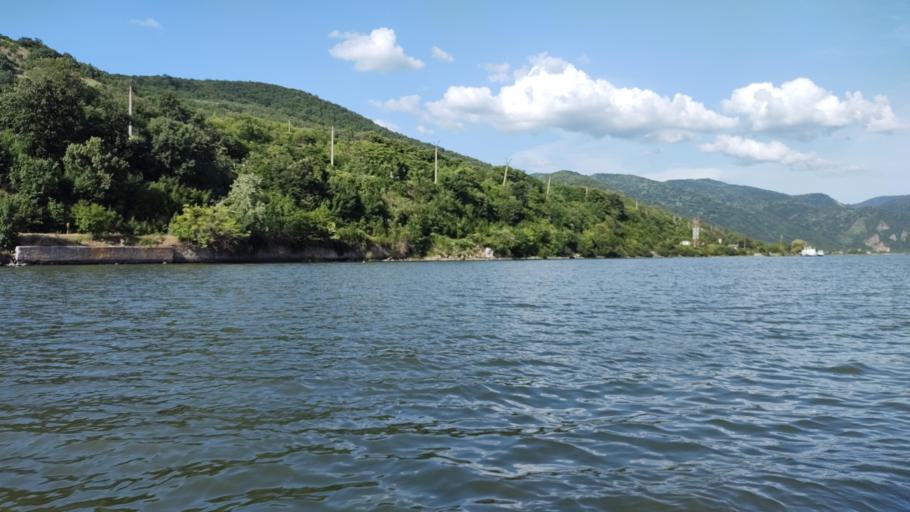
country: RO
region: Caras-Severin
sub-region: Comuna Berzasca
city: Berzasca
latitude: 44.6371
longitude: 21.9584
